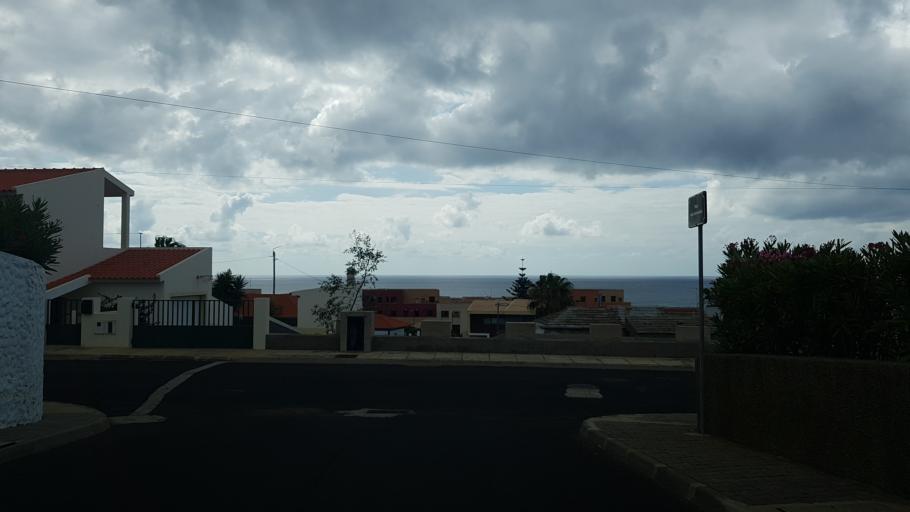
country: PT
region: Madeira
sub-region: Porto Santo
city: Vila de Porto Santo
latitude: 33.0409
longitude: -16.3612
